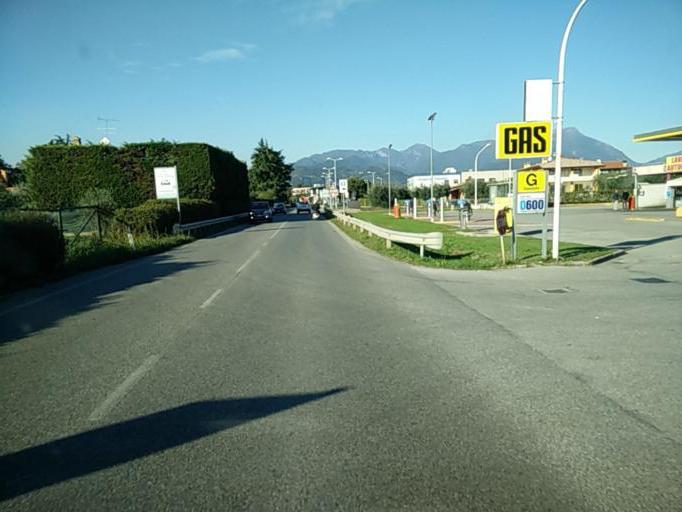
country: IT
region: Lombardy
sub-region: Provincia di Brescia
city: Raffa
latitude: 45.5627
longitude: 10.5323
